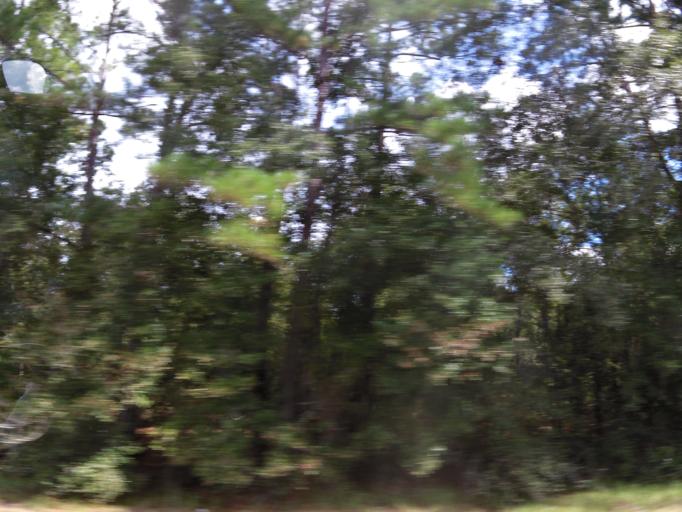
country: US
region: Georgia
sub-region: Brantley County
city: Nahunta
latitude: 31.1036
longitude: -82.0046
